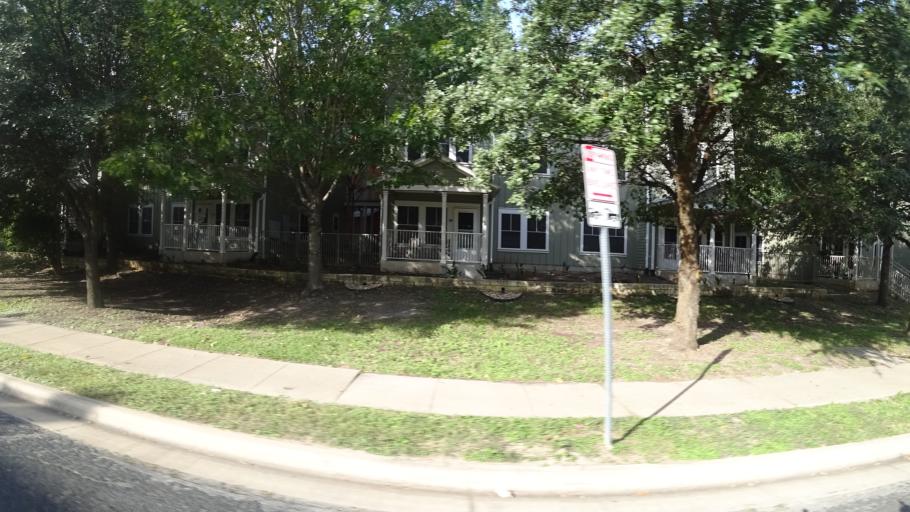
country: US
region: Texas
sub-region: Travis County
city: Austin
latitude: 30.2646
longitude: -97.7083
